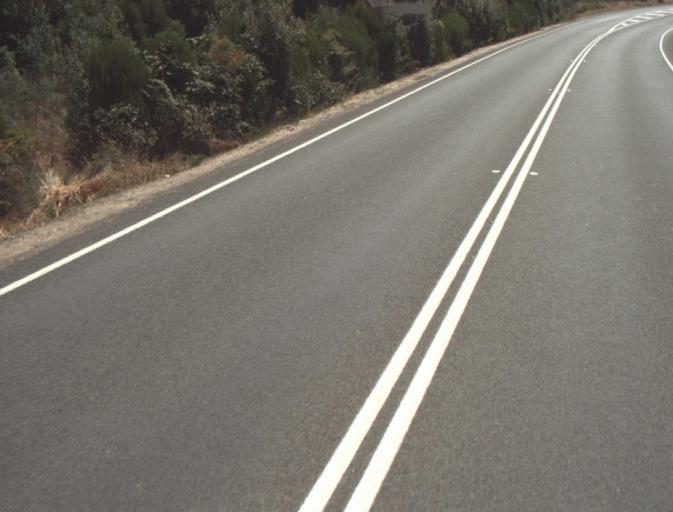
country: AU
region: Tasmania
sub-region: Launceston
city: Mayfield
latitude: -41.3614
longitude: 147.1436
